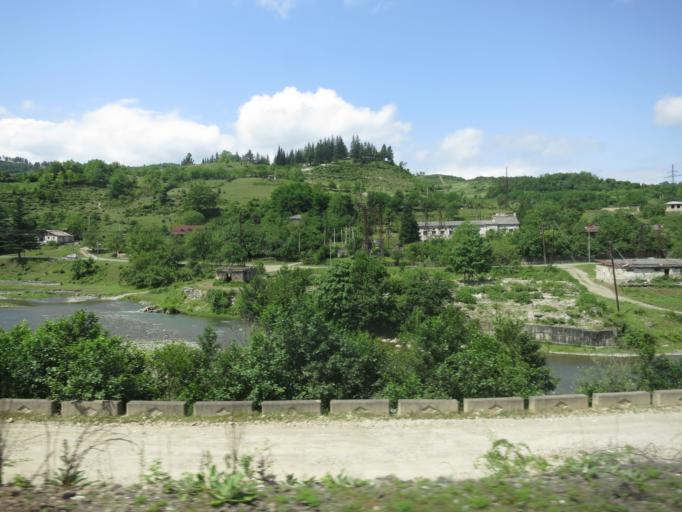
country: GE
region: Imereti
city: Kharagauli
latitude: 42.0266
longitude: 43.1983
